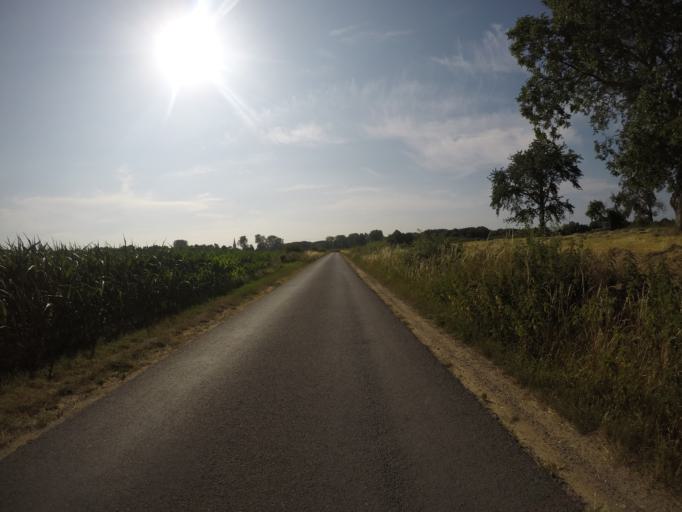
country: DE
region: North Rhine-Westphalia
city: Kalkar
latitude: 51.7376
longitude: 6.3068
